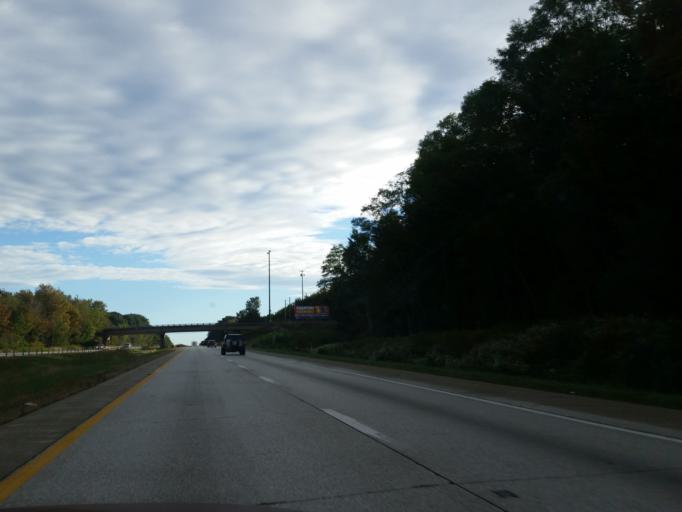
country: US
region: Pennsylvania
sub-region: Erie County
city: Northwest Harborcreek
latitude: 42.1071
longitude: -79.9808
